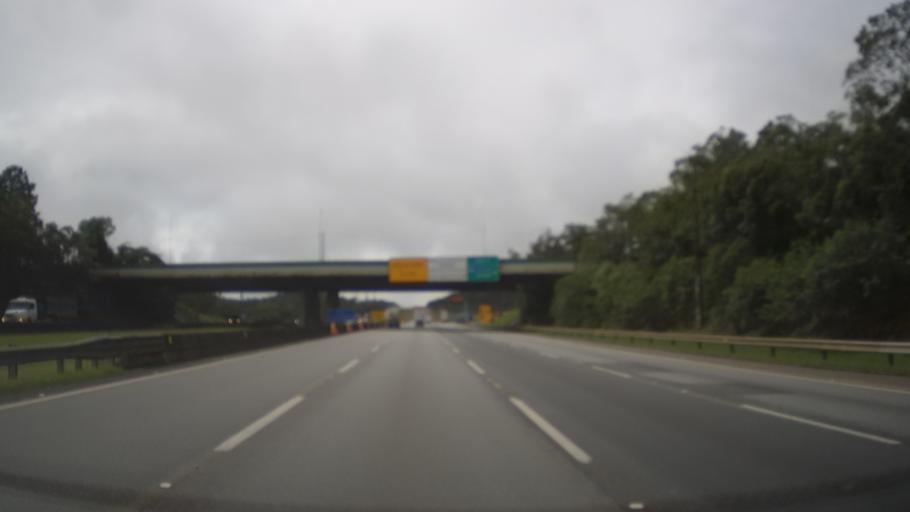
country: BR
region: Sao Paulo
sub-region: Cubatao
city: Cubatao
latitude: -23.8922
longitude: -46.5645
